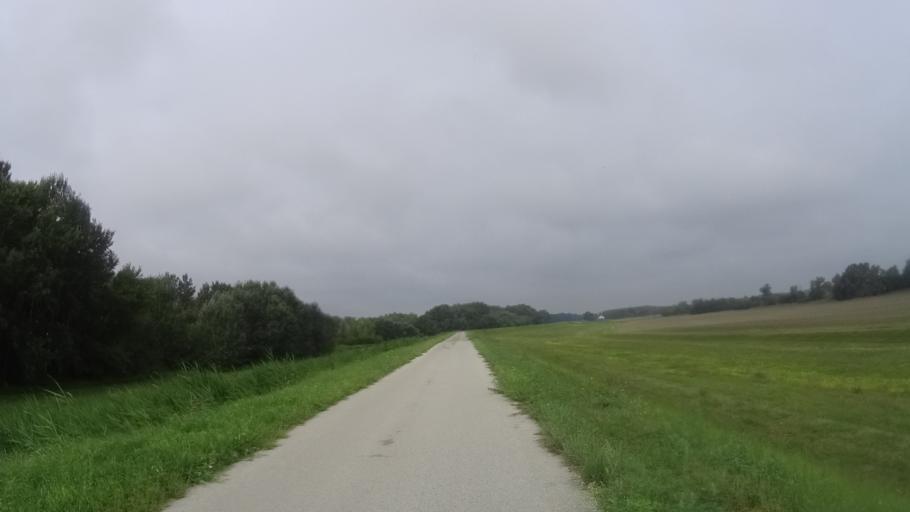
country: SK
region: Nitriansky
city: Komarno
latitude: 47.7451
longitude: 18.1720
